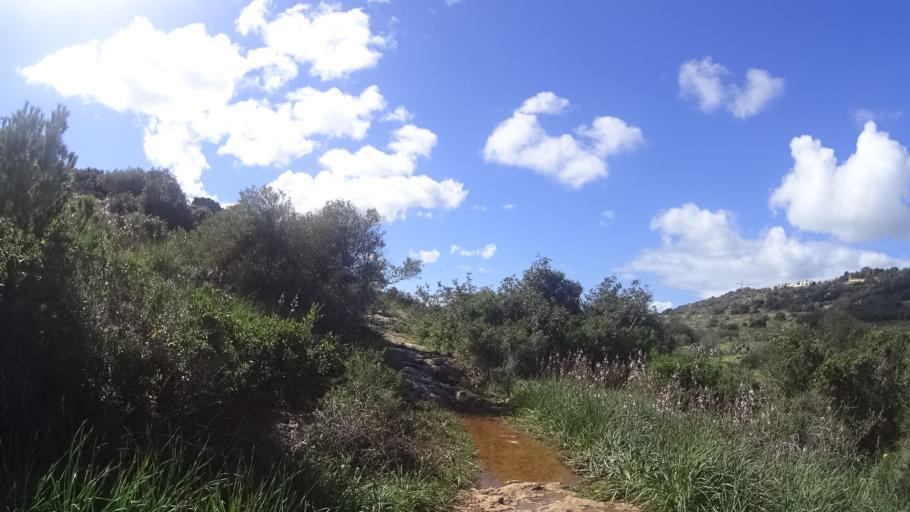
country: MT
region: Il-Mellieha
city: Mellieha
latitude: 35.9524
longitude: 14.3802
